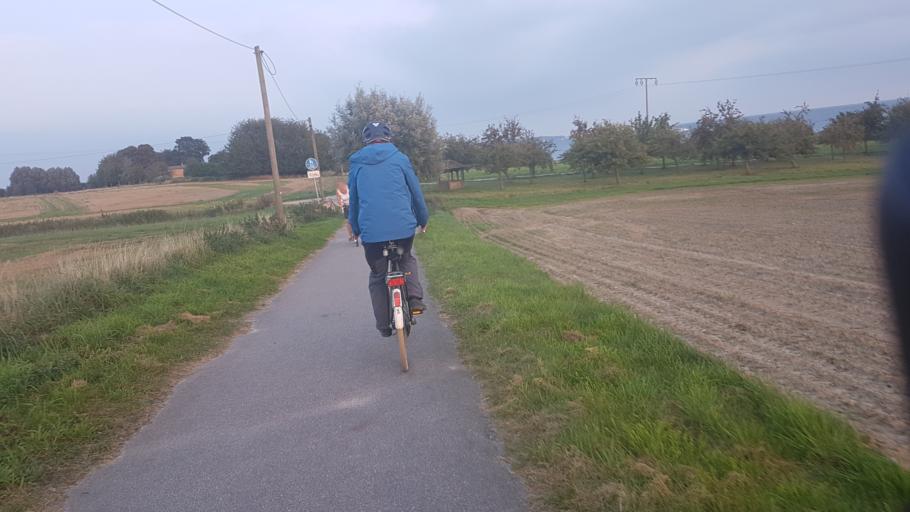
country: DE
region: Mecklenburg-Vorpommern
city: Putbus
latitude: 54.3421
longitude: 13.5493
